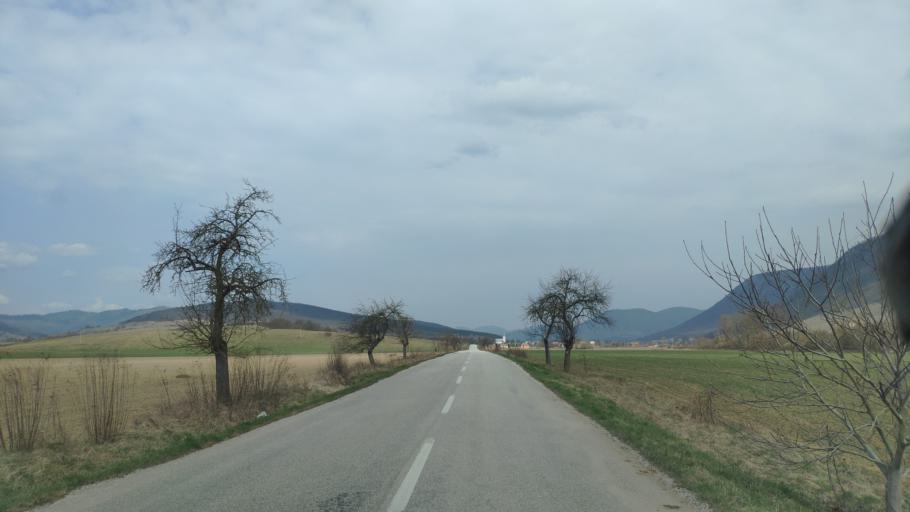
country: SK
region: Kosicky
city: Roznava
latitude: 48.5960
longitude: 20.3840
